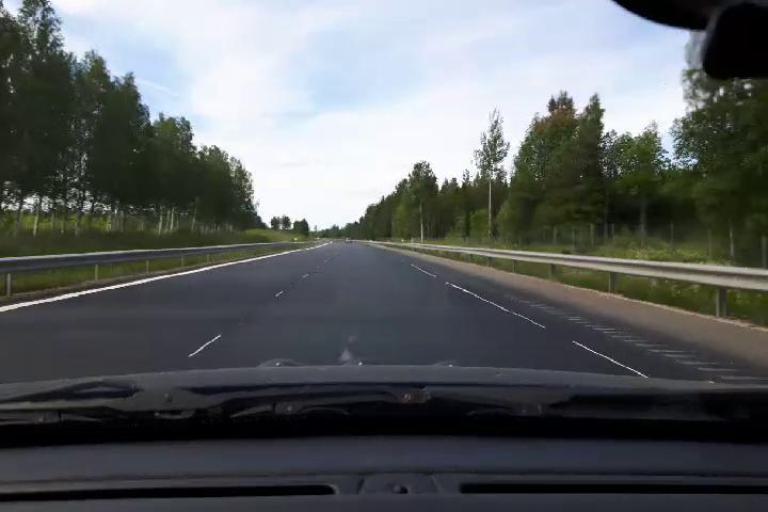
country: SE
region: Gaevleborg
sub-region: Gavle Kommun
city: Gavle
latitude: 60.5774
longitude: 17.2224
